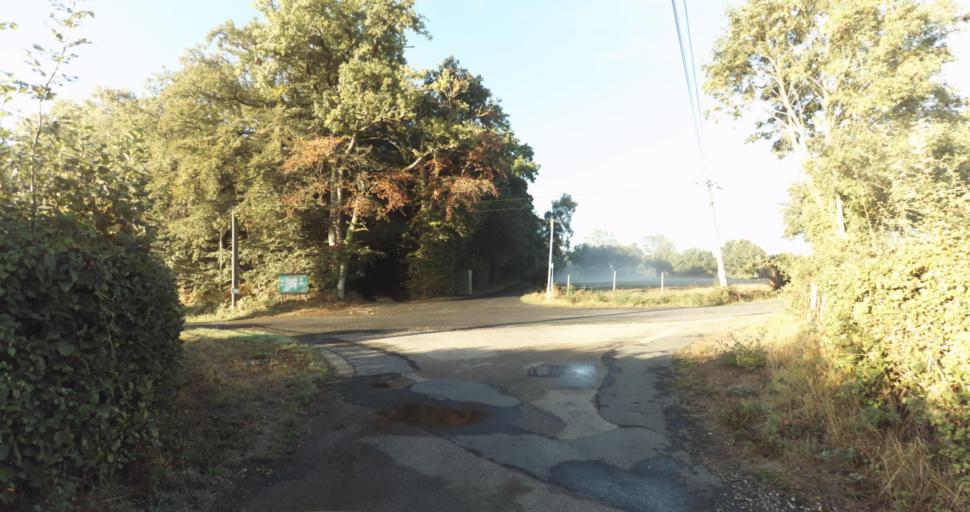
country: FR
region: Lower Normandy
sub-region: Departement de l'Orne
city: Vimoutiers
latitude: 48.9115
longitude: 0.1510
